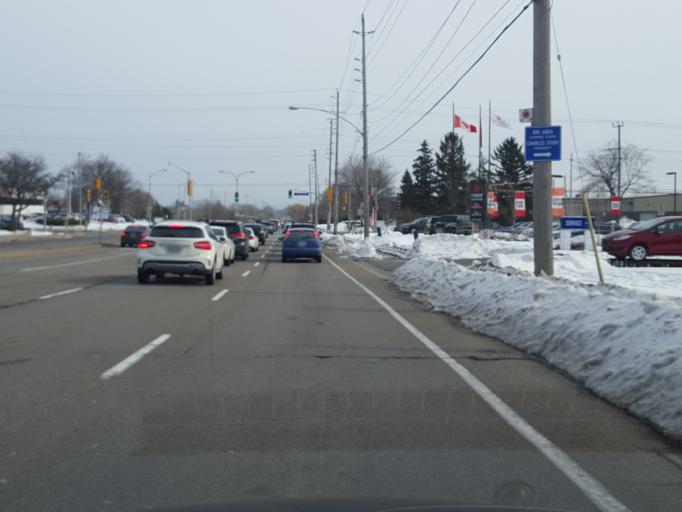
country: CA
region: Ontario
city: Burlington
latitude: 43.3638
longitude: -79.7845
